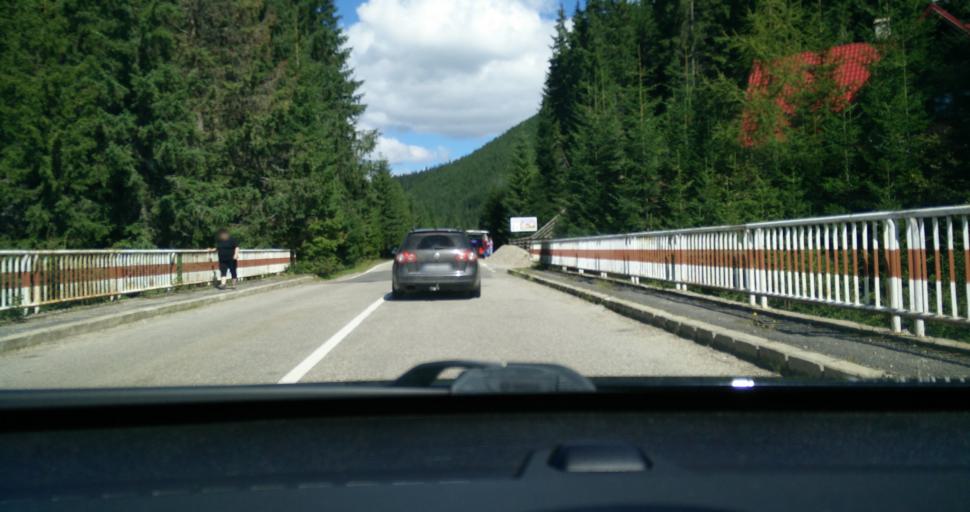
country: RO
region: Alba
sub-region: Comuna Sugag
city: Sugag
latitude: 45.5407
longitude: 23.6383
